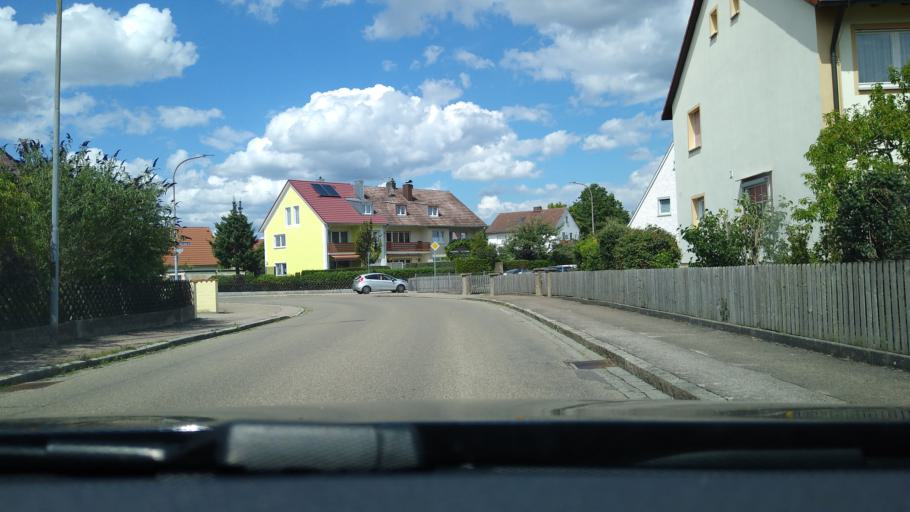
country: DE
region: Bavaria
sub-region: Regierungsbezirk Mittelfranken
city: Gunzenhausen
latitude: 49.1215
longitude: 10.7662
